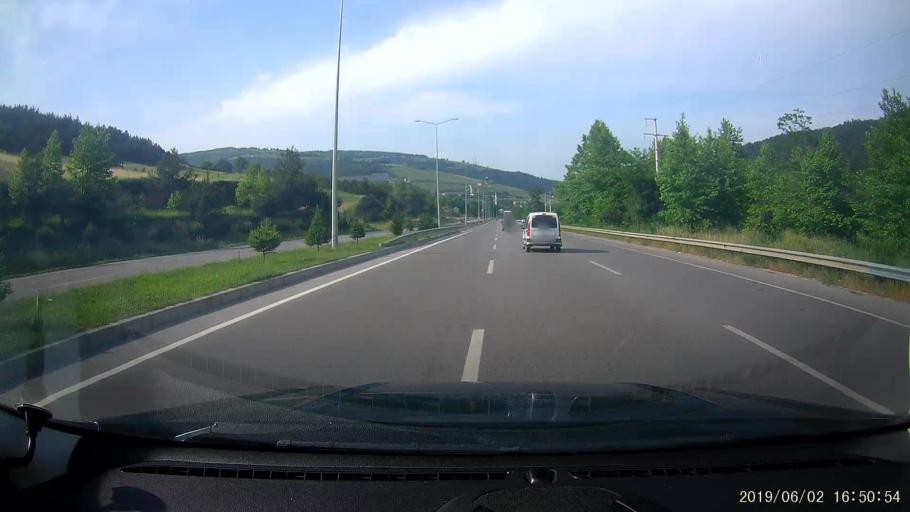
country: TR
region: Samsun
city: Taflan
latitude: 41.2645
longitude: 36.1765
